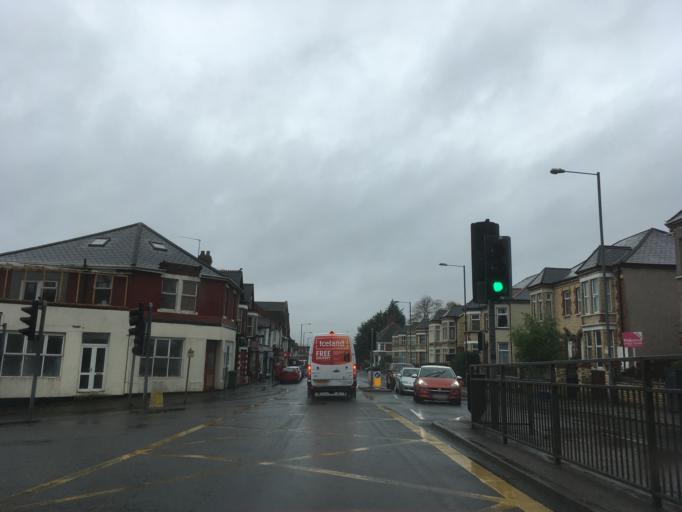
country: GB
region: Wales
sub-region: Newport
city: Caerleon
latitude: 51.5882
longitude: -2.9626
